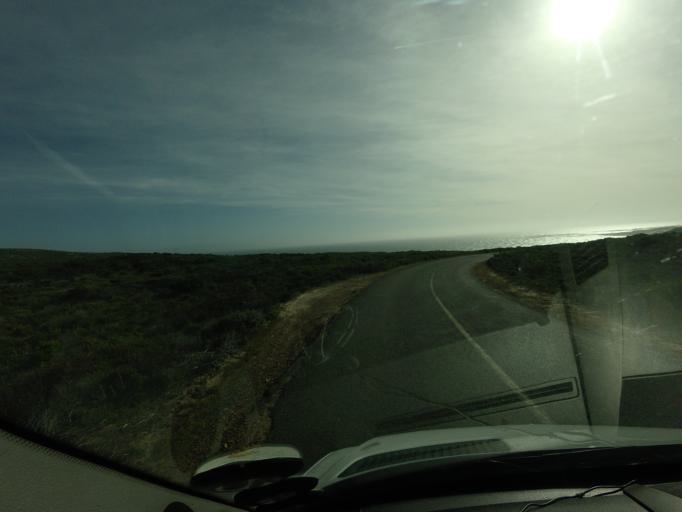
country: ZA
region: Western Cape
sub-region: City of Cape Town
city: Retreat
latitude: -34.3378
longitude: 18.4643
